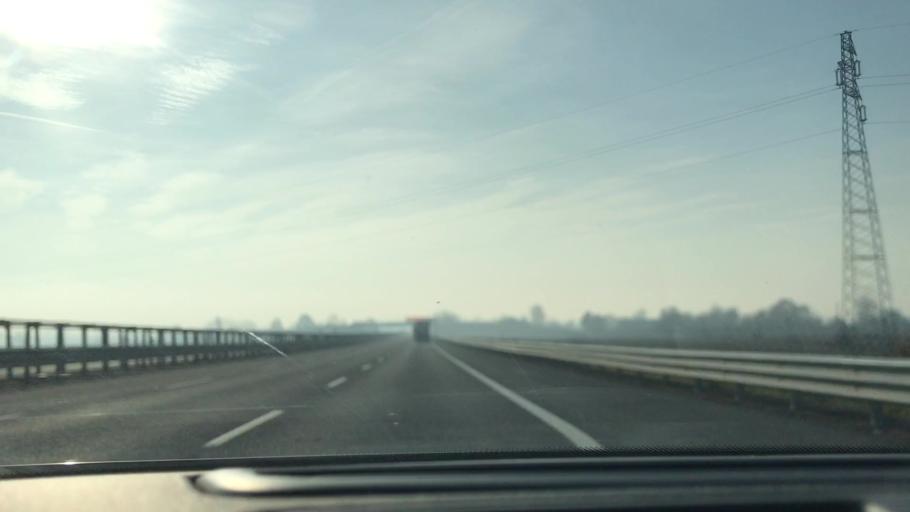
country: IT
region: Piedmont
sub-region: Provincia di Alessandria
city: Alessandria
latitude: 44.8927
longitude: 8.5687
